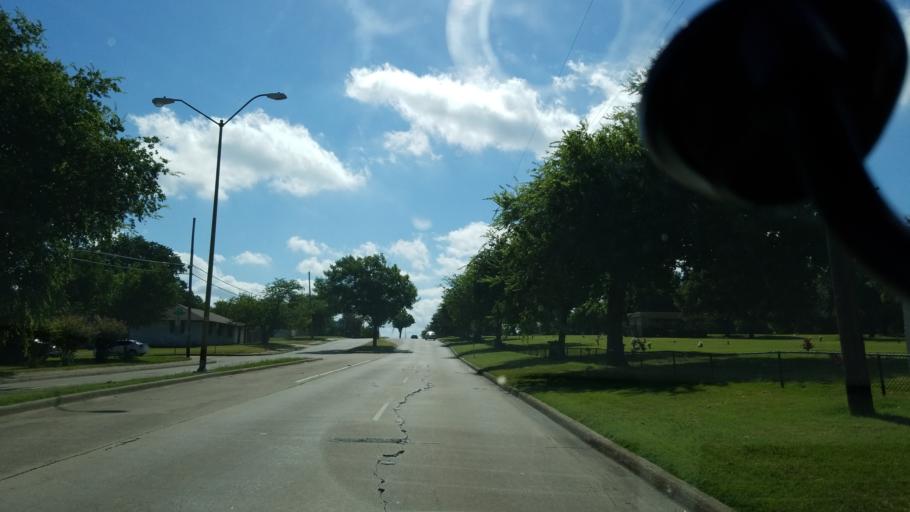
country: US
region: Texas
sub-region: Dallas County
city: Cockrell Hill
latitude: 32.6750
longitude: -96.8177
